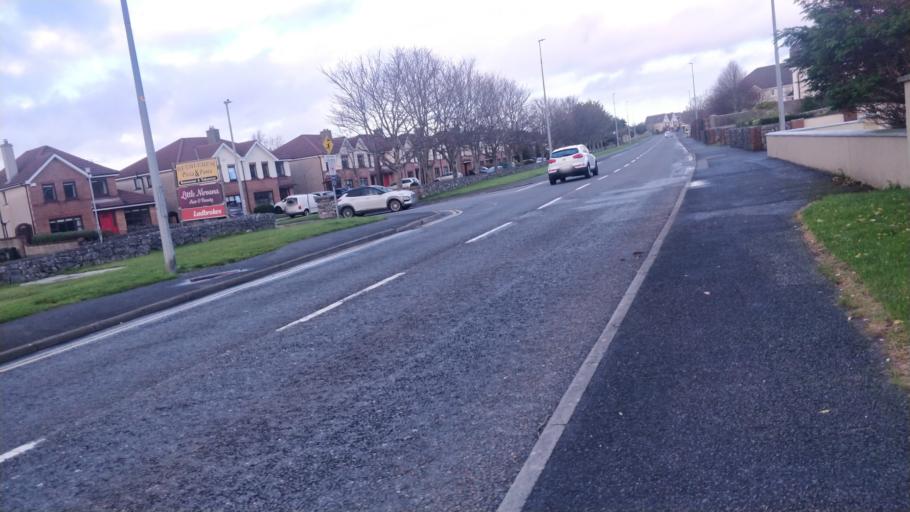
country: IE
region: Connaught
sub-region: County Galway
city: Gaillimh
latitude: 53.2890
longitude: -8.9999
